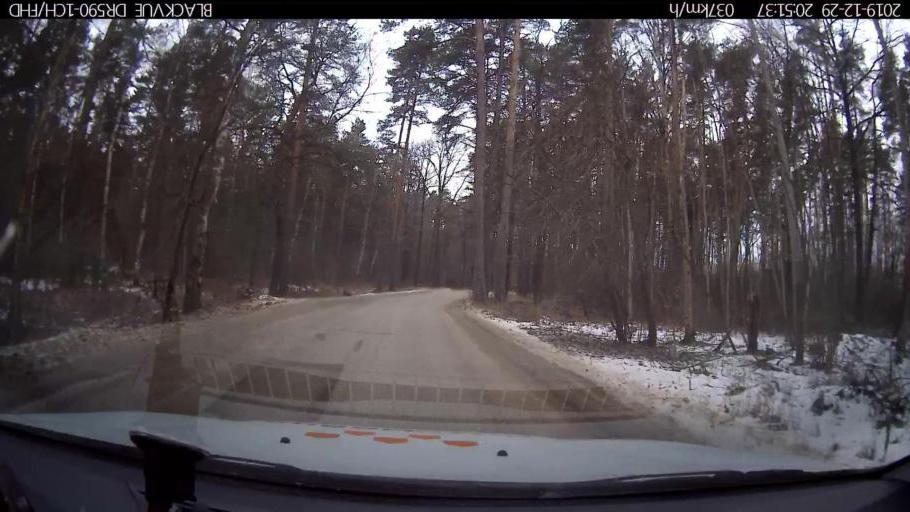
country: RU
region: Nizjnij Novgorod
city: Afonino
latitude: 56.1779
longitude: 44.0005
